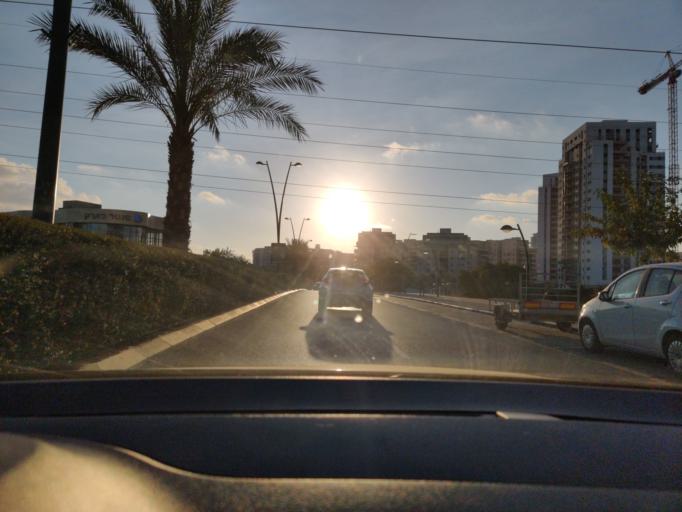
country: IL
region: Central District
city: Elyakhin
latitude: 32.4275
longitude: 34.9346
